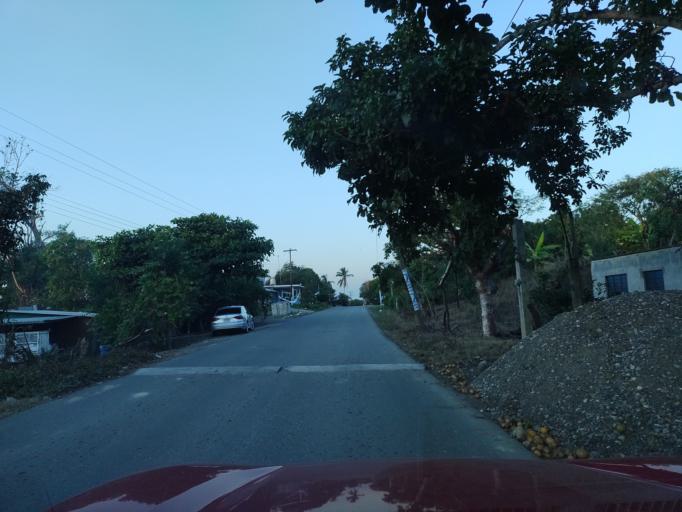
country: MX
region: Veracruz
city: Agua Dulce
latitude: 20.3230
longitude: -97.2700
